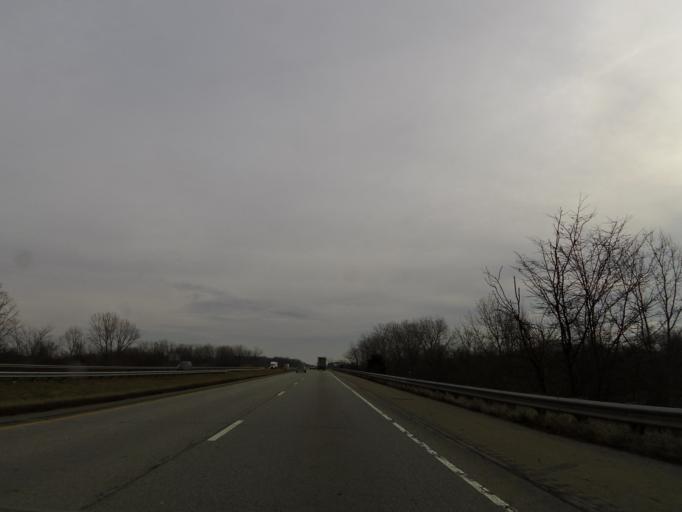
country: US
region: Indiana
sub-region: Fountain County
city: Veedersburg
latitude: 40.1238
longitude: -87.2575
